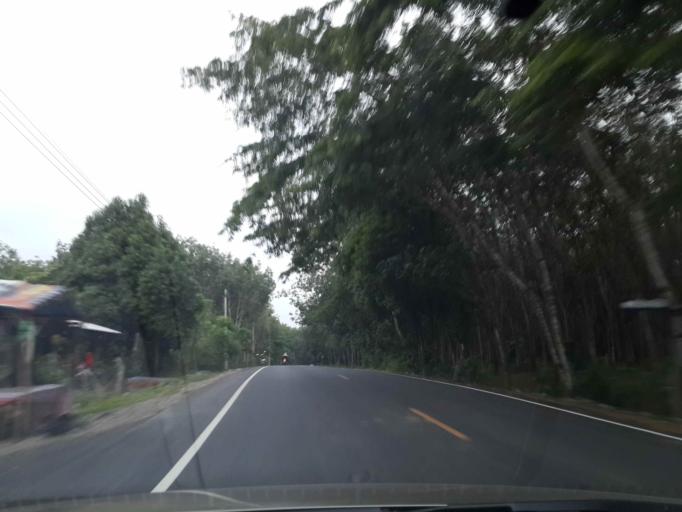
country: TH
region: Narathiwat
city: Rueso
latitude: 6.3519
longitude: 101.4732
